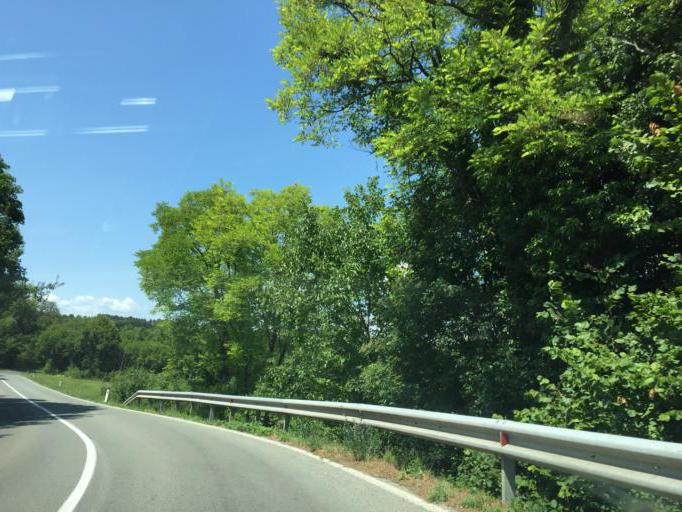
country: SI
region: Sezana
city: Sezana
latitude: 45.7199
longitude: 13.8666
